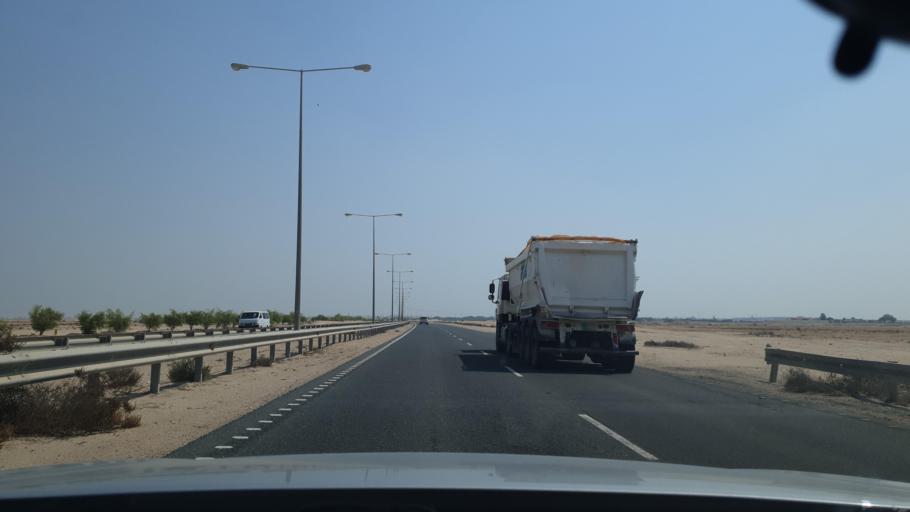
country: QA
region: Al Khawr
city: Al Khawr
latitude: 25.7417
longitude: 51.4855
